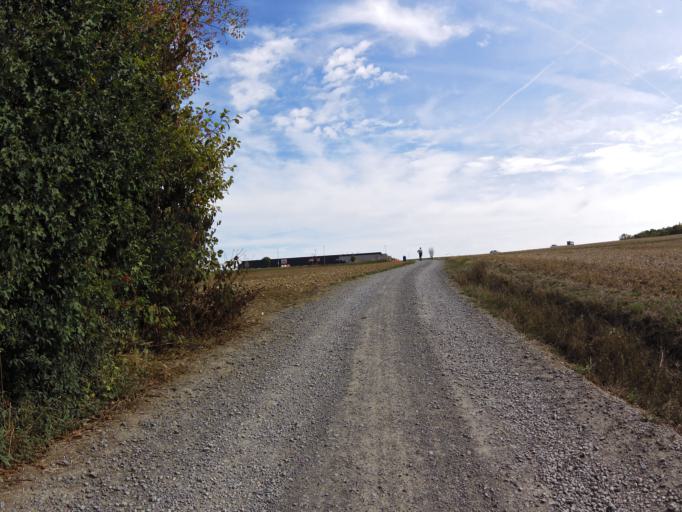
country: DE
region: Bavaria
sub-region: Regierungsbezirk Unterfranken
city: Wuerzburg
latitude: 49.7691
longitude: 9.8600
